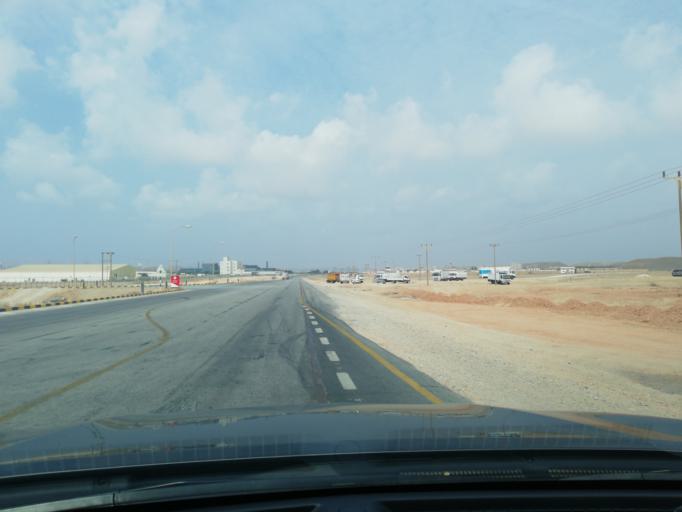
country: OM
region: Zufar
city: Salalah
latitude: 16.9505
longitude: 53.9840
